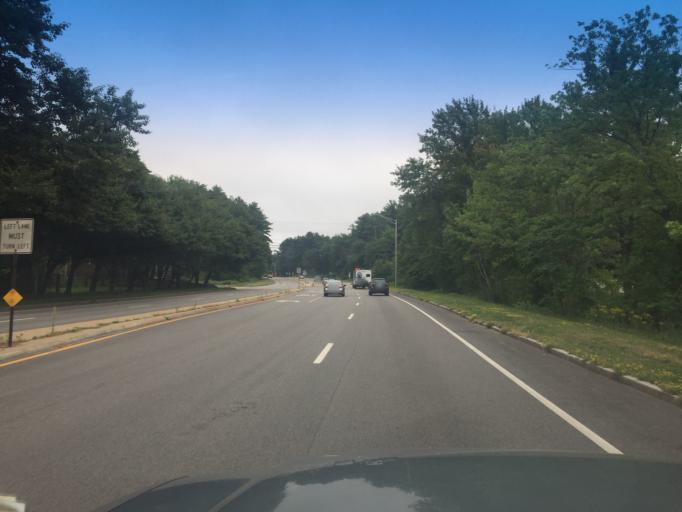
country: US
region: New Hampshire
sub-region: Rockingham County
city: Portsmouth
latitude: 43.0848
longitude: -70.7807
